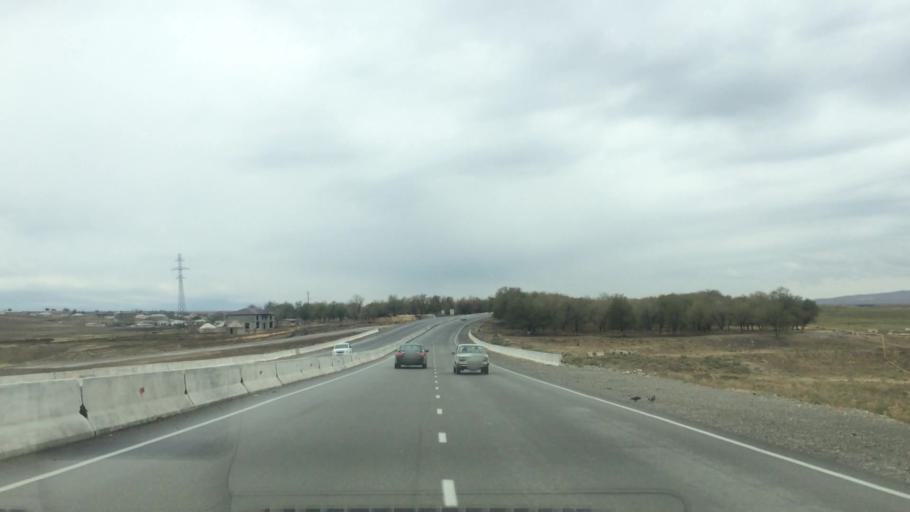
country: UZ
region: Samarqand
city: Bulung'ur
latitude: 39.9210
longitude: 67.5162
